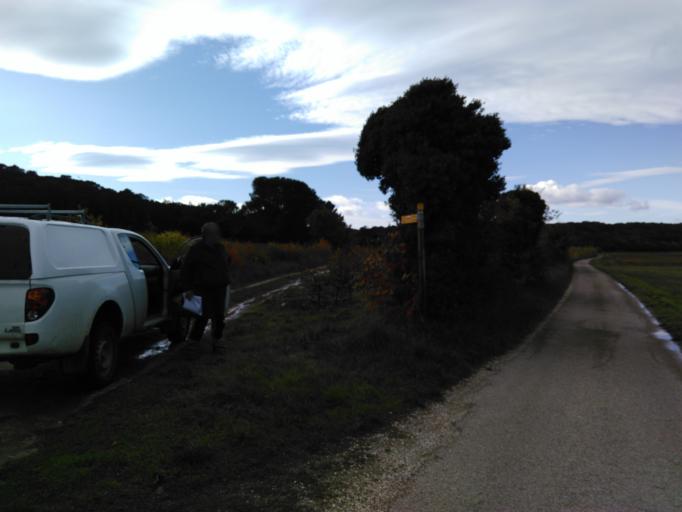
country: FR
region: Provence-Alpes-Cote d'Azur
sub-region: Departement du Vaucluse
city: Uchaux
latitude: 44.2310
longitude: 4.7881
